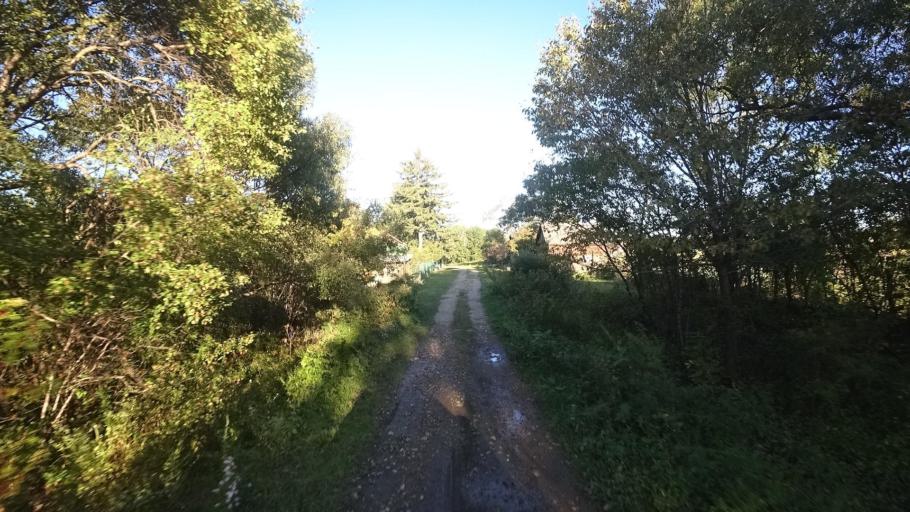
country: RU
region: Primorskiy
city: Kirovskiy
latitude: 44.8349
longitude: 133.5737
